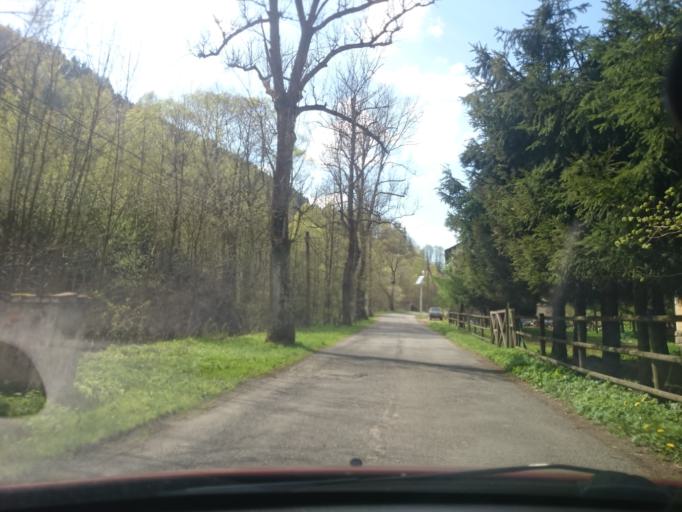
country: PL
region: Lower Silesian Voivodeship
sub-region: Powiat klodzki
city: Bystrzyca Klodzka
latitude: 50.2980
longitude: 16.5451
